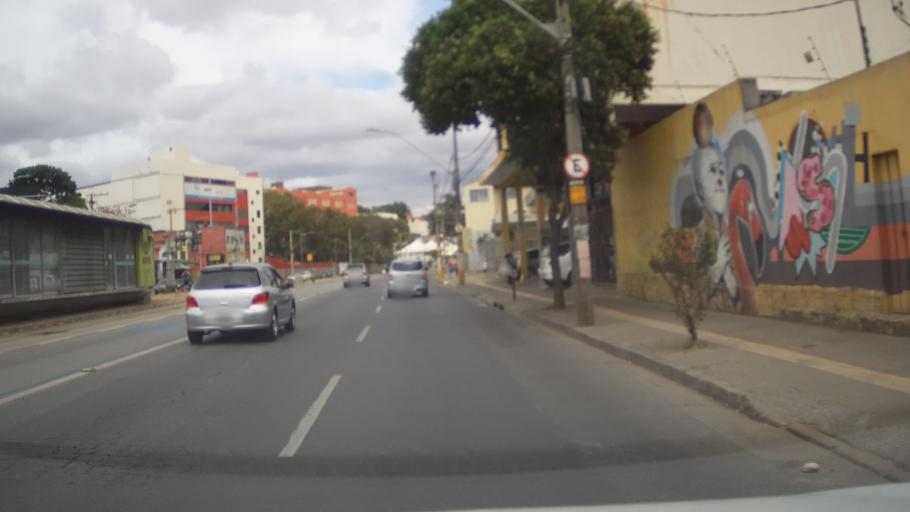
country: BR
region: Minas Gerais
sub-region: Belo Horizonte
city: Belo Horizonte
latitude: -19.8120
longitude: -43.9604
